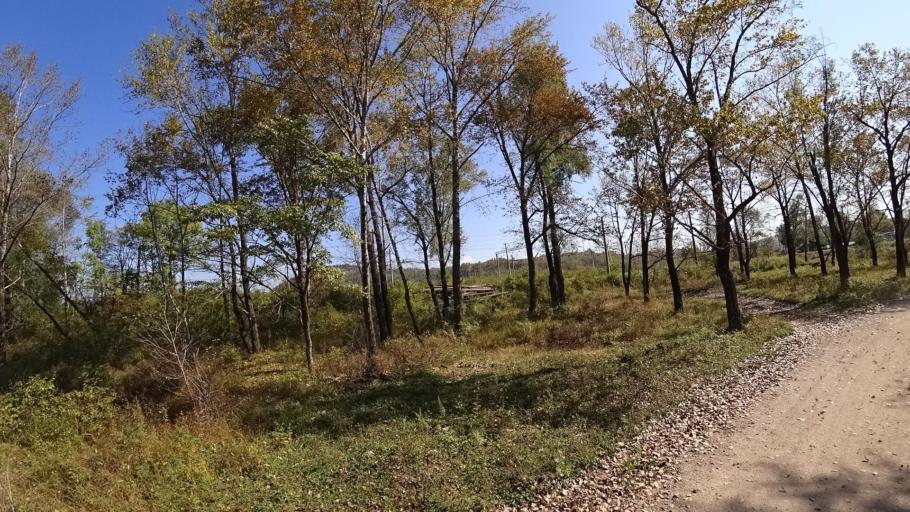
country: RU
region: Jewish Autonomous Oblast
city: Bira
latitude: 49.0020
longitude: 132.4506
